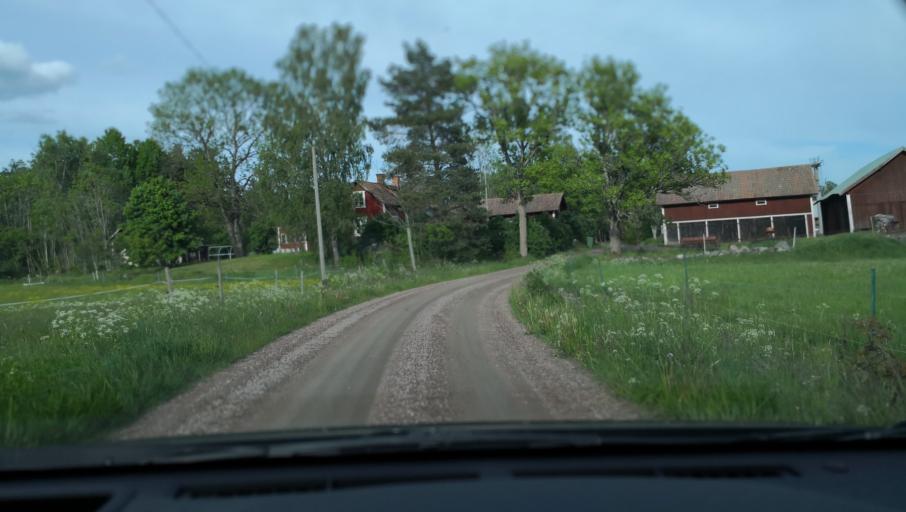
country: SE
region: Vaestmanland
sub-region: Kungsors Kommun
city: Kungsoer
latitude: 59.3616
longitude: 16.0468
